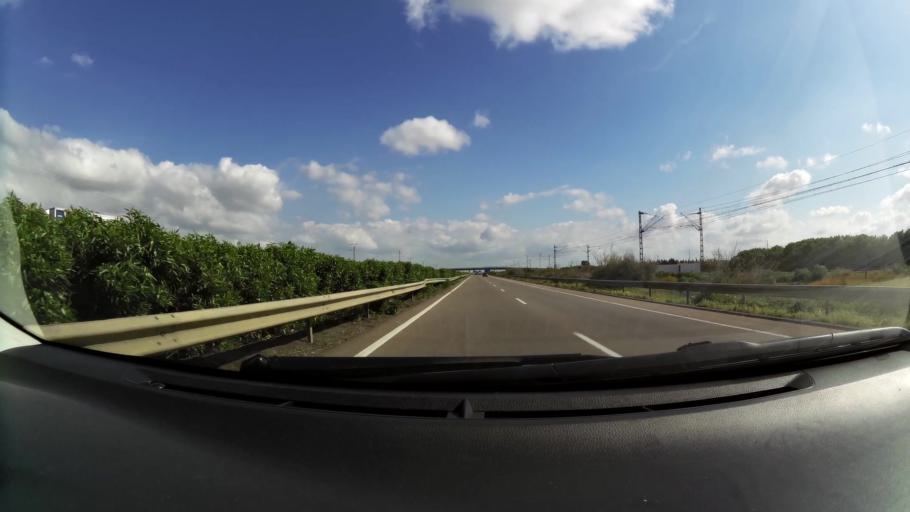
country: MA
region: Chaouia-Ouardigha
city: Nouaseur
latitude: 33.3378
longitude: -7.6113
